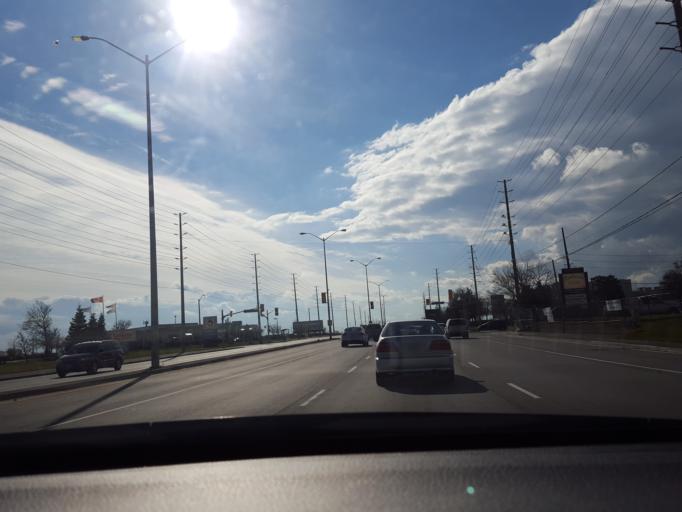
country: CA
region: Ontario
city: Brampton
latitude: 43.6810
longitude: -79.6679
